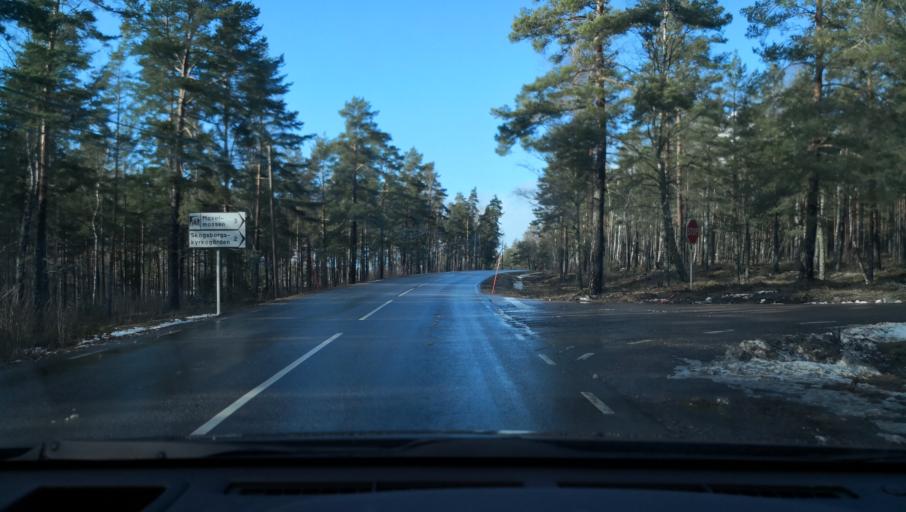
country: SE
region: Vaestmanland
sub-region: Arboga Kommun
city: Arboga
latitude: 59.3746
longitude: 15.8428
